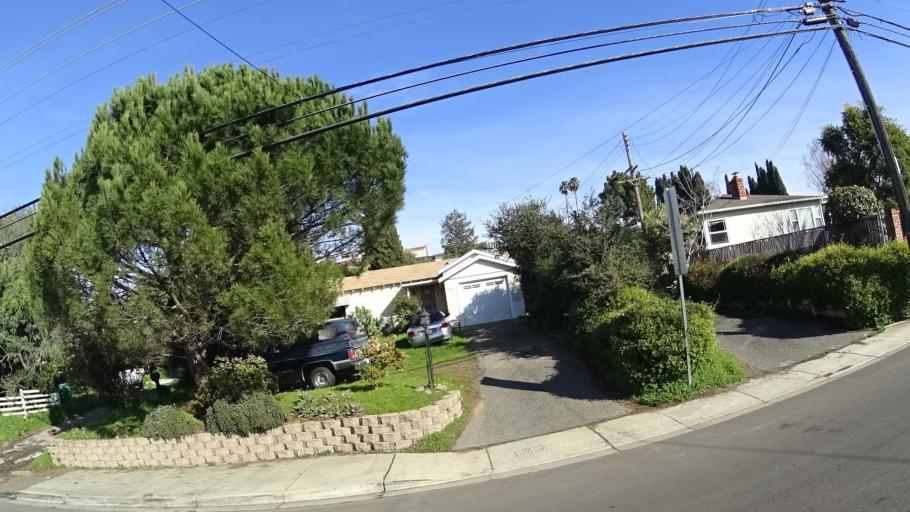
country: US
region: California
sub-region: Alameda County
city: Fairview
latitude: 37.6794
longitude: -122.0510
